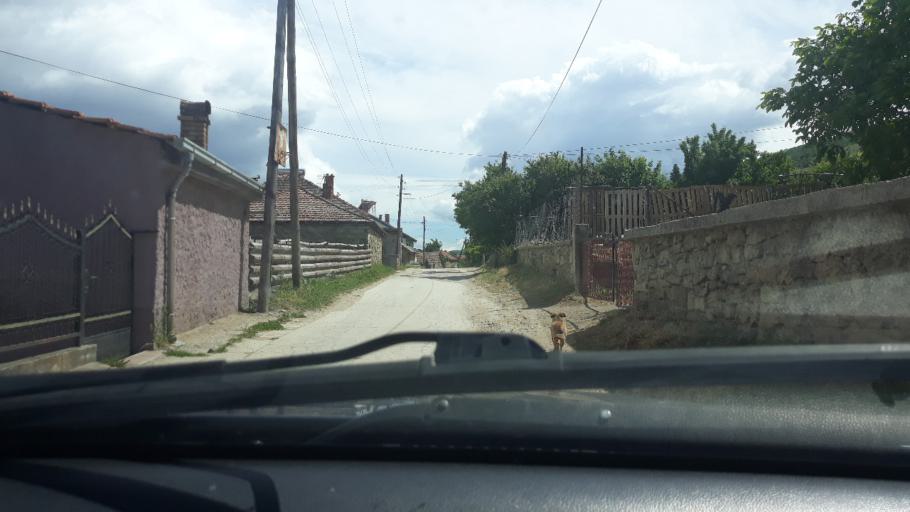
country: MK
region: Krivogastani
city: Krivogashtani
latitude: 41.3236
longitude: 21.3044
